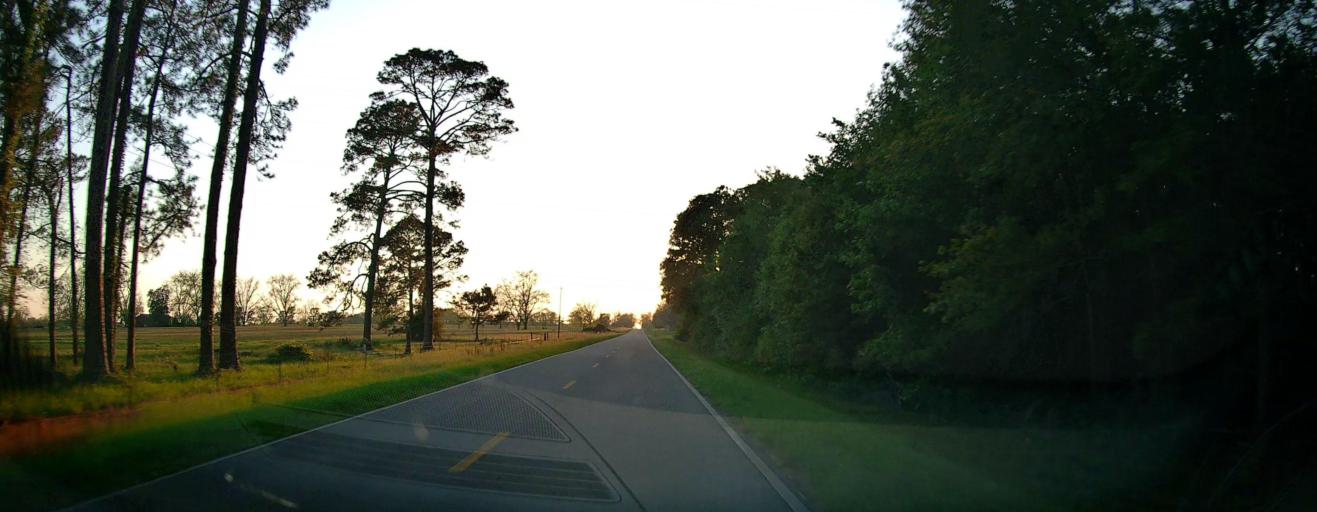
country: US
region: Georgia
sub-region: Ben Hill County
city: Fitzgerald
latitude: 31.7179
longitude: -83.2998
